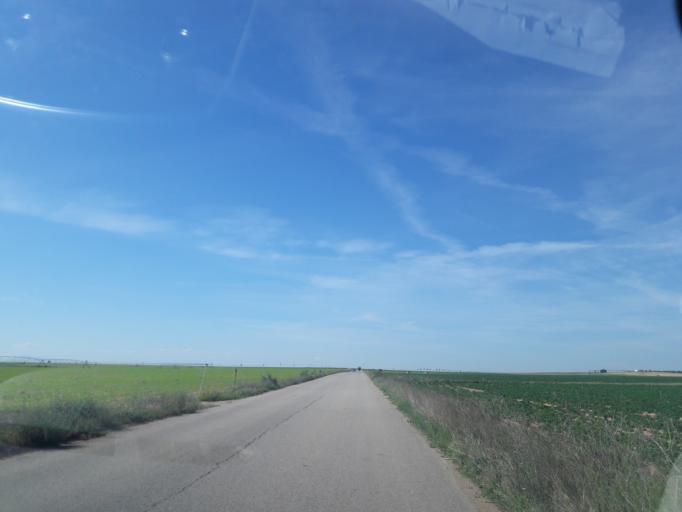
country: ES
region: Castille and Leon
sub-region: Provincia de Salamanca
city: Villoruela
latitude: 41.0278
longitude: -5.3915
